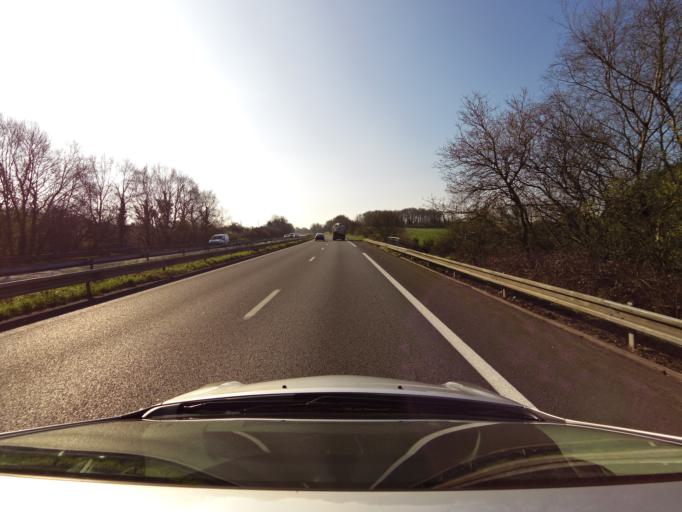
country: FR
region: Brittany
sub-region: Departement du Morbihan
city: Gestel
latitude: 47.7977
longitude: -3.4547
